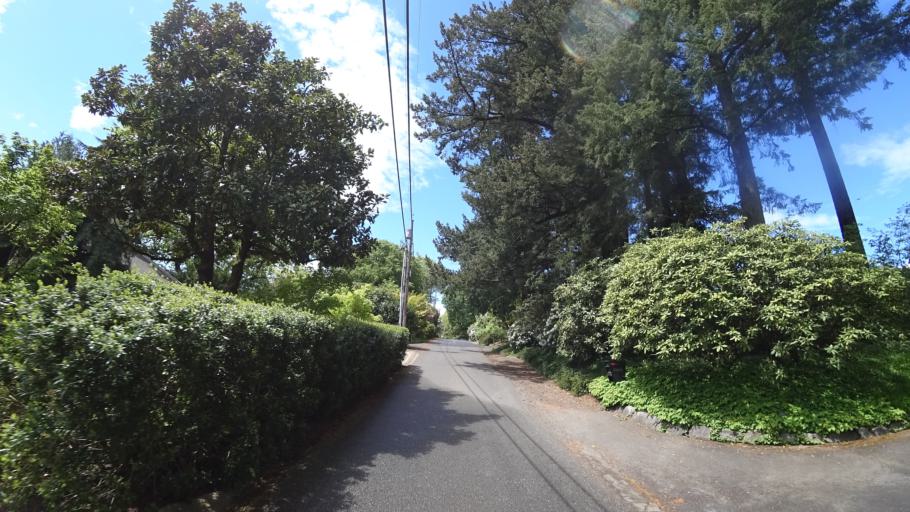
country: US
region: Oregon
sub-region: Washington County
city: West Slope
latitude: 45.5050
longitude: -122.7301
